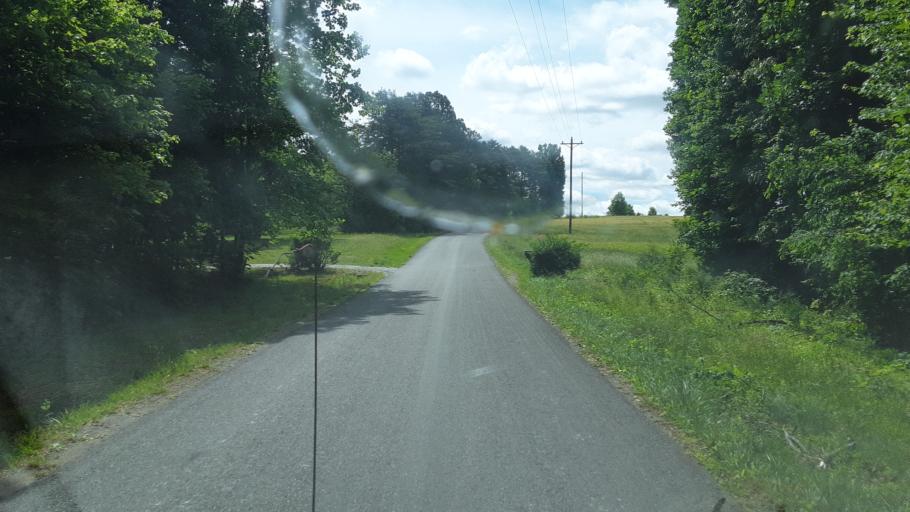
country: US
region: Virginia
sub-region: Pittsylvania County
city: Chatham
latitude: 36.8442
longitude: -79.4475
